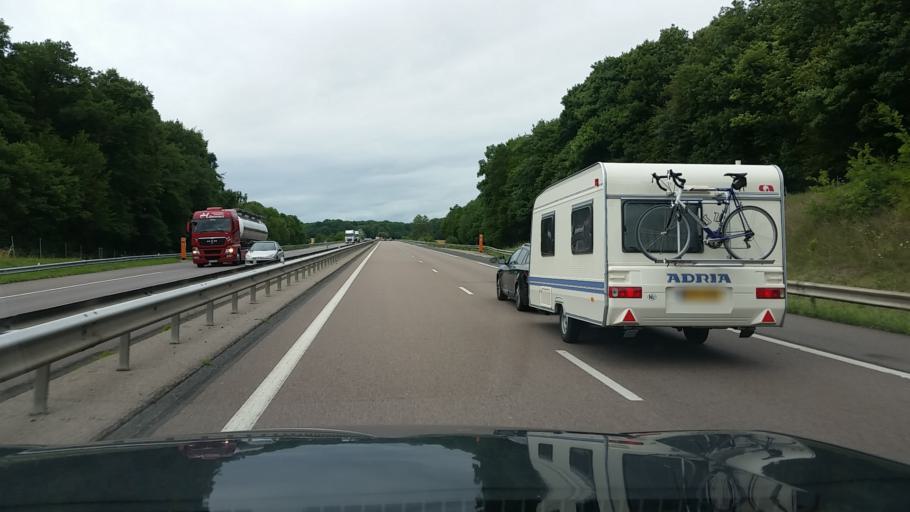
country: FR
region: Lorraine
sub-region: Departement des Vosges
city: Chatenois
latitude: 48.3053
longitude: 5.8565
